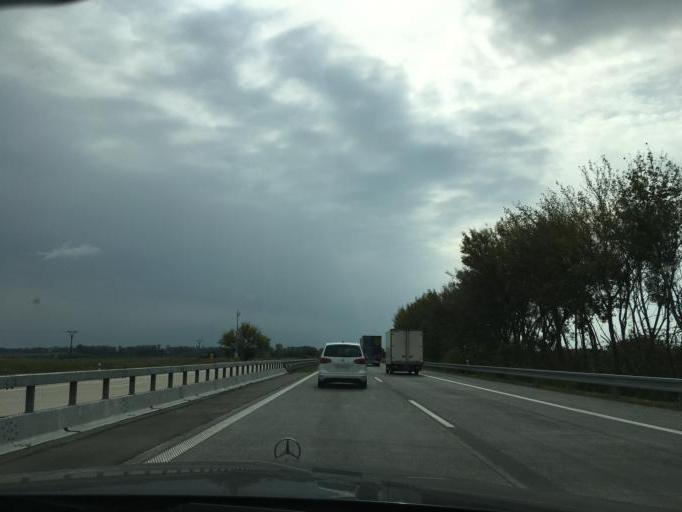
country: CZ
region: South Moravian
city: Podivin
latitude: 48.8430
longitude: 16.8569
